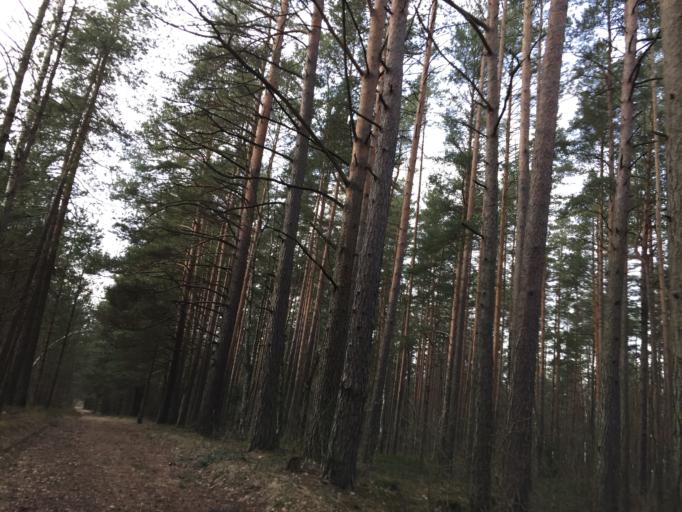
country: LV
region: Stopini
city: Ulbroka
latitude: 56.9213
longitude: 24.3053
